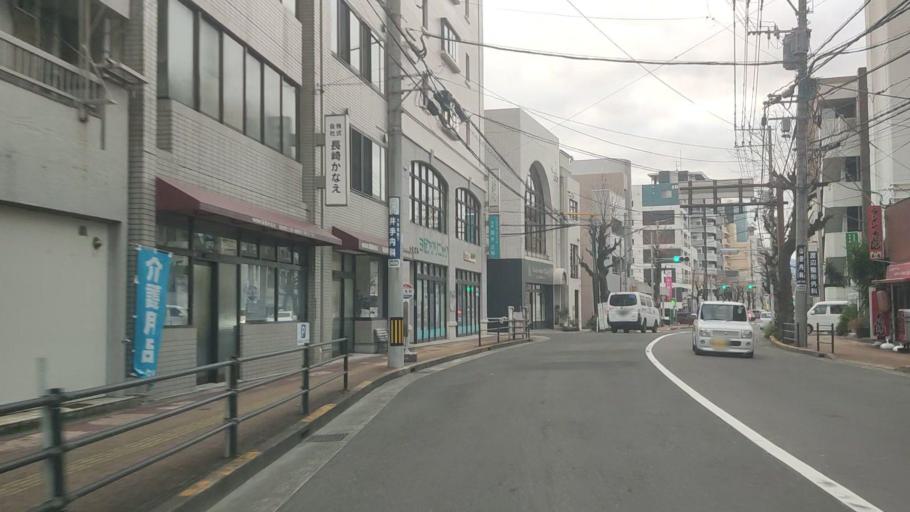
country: JP
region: Nagasaki
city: Nagasaki-shi
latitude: 32.7686
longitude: 129.8667
